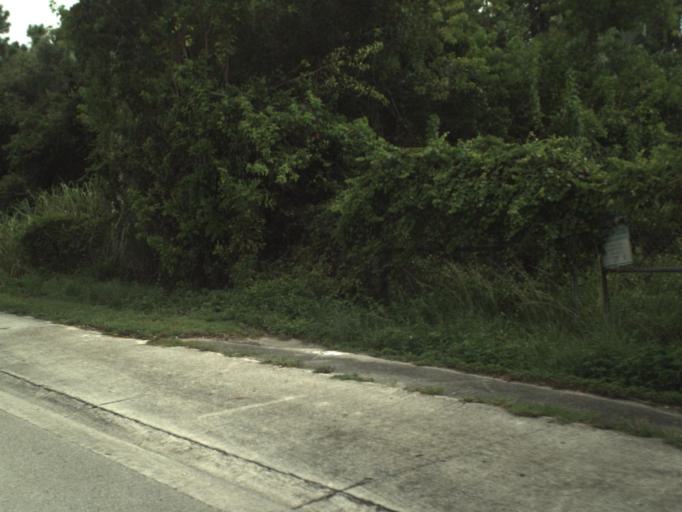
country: US
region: Florida
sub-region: Palm Beach County
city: Atlantis
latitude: 26.5870
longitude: -80.1134
